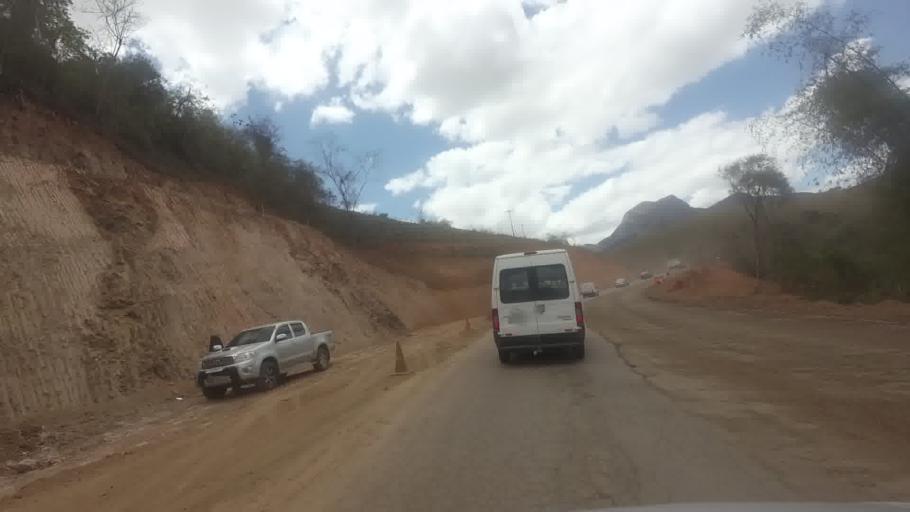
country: BR
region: Rio de Janeiro
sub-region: Santo Antonio De Padua
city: Santo Antonio de Padua
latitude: -21.5144
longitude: -42.0952
